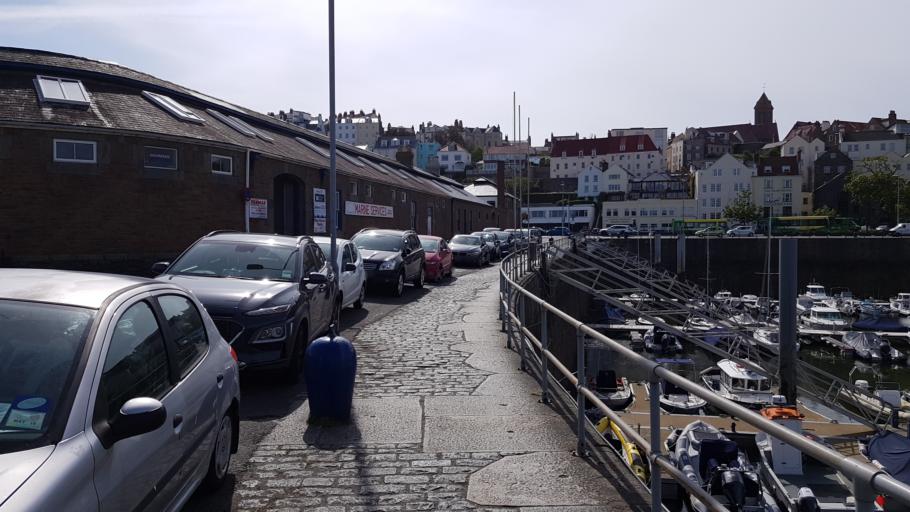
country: GG
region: St Peter Port
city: Saint Peter Port
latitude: 49.4527
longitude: -2.5339
